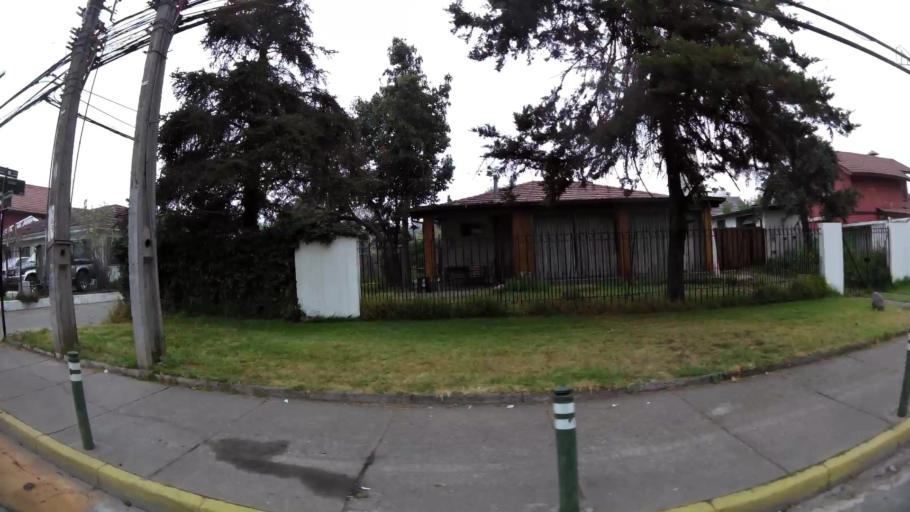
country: CL
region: Santiago Metropolitan
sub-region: Provincia de Santiago
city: Villa Presidente Frei, Nunoa, Santiago, Chile
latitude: -33.3902
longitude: -70.5593
